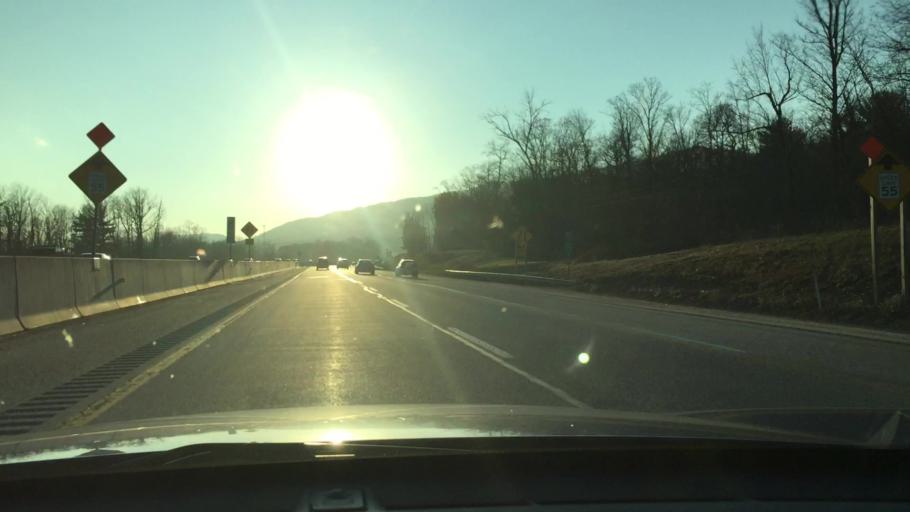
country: US
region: Pennsylvania
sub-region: Franklin County
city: Doylestown
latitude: 40.1553
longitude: -77.6204
